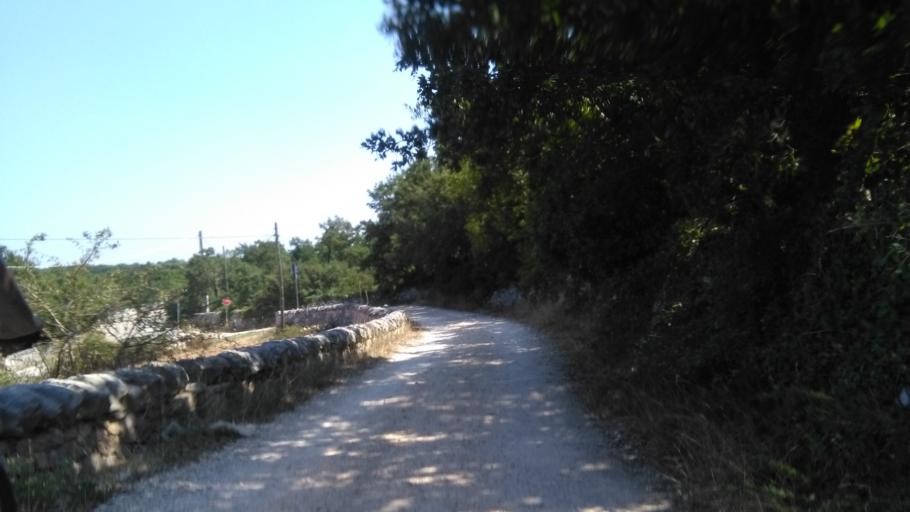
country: IT
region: Apulia
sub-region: Provincia di Bari
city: Alberobello
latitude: 40.8043
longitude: 17.2062
